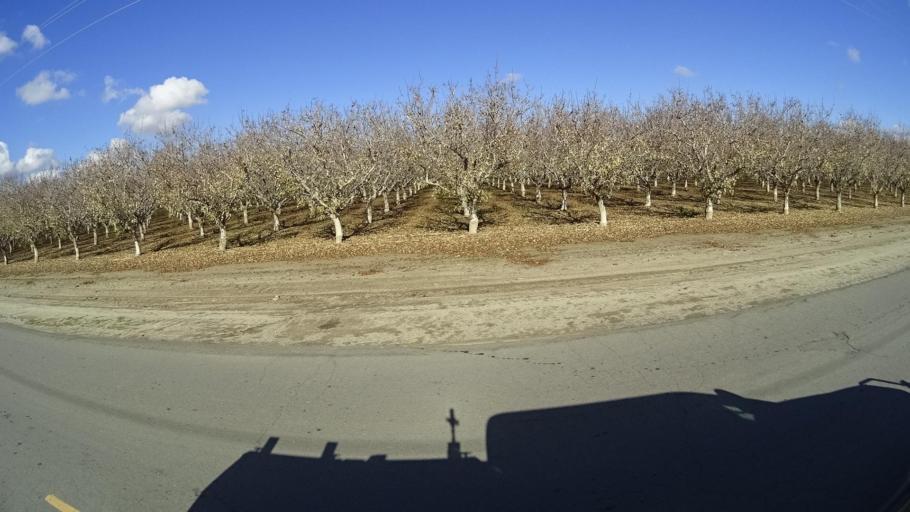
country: US
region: California
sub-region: Kern County
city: McFarland
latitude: 35.6885
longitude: -119.2962
